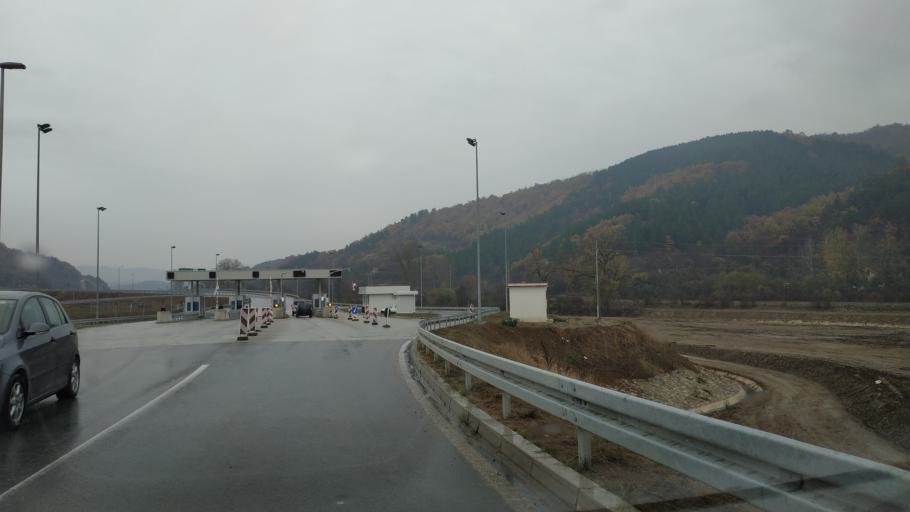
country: RS
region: Central Serbia
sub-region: Pirotski Okrug
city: Pirot
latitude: 43.1875
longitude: 22.5668
